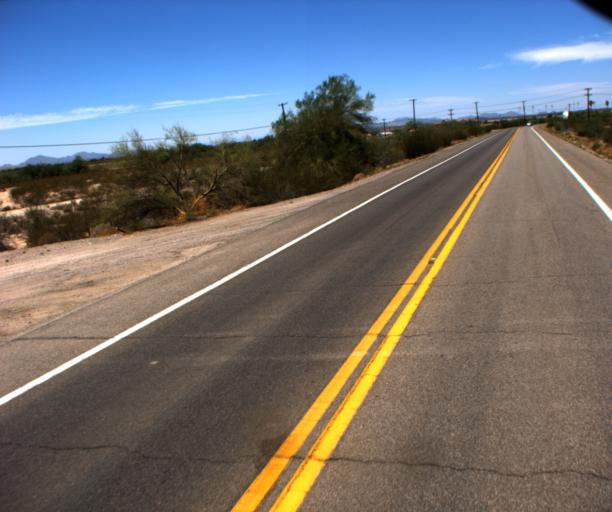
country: US
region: Arizona
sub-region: Pinal County
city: Florence
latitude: 33.0157
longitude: -111.3838
